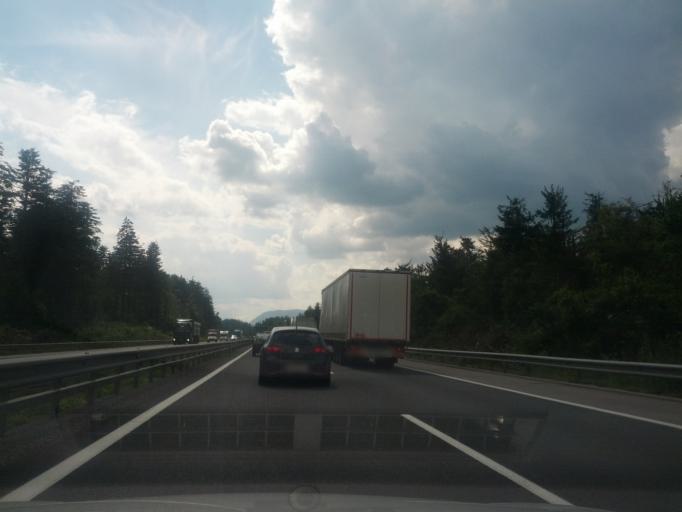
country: SI
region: Postojna
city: Postojna
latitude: 45.7978
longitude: 14.2474
